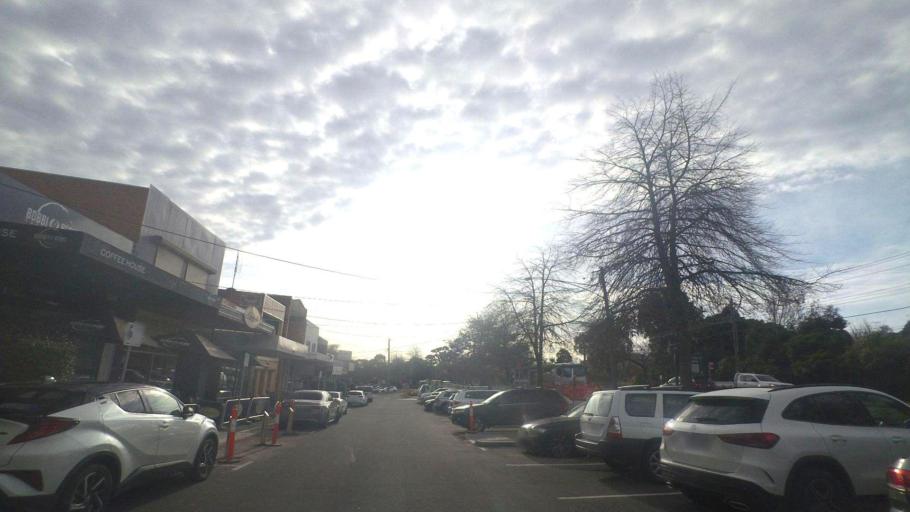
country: AU
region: Victoria
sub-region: Boroondara
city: Balwyn North
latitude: -37.7847
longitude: 145.0774
